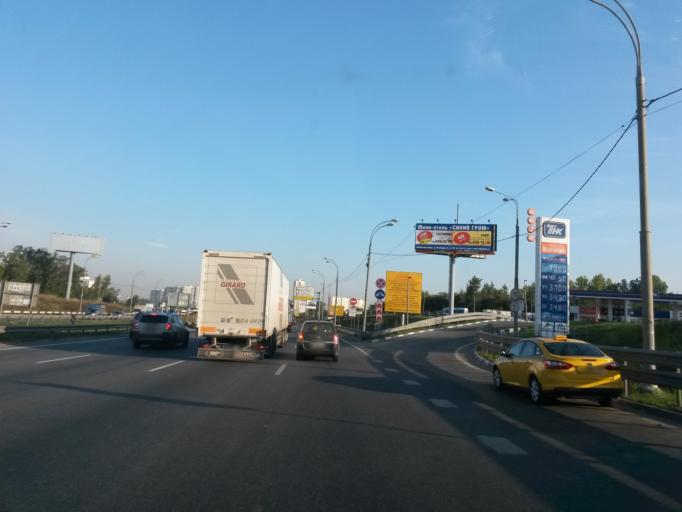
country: RU
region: Moscow
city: Biryulevo
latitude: 55.5697
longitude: 37.6931
